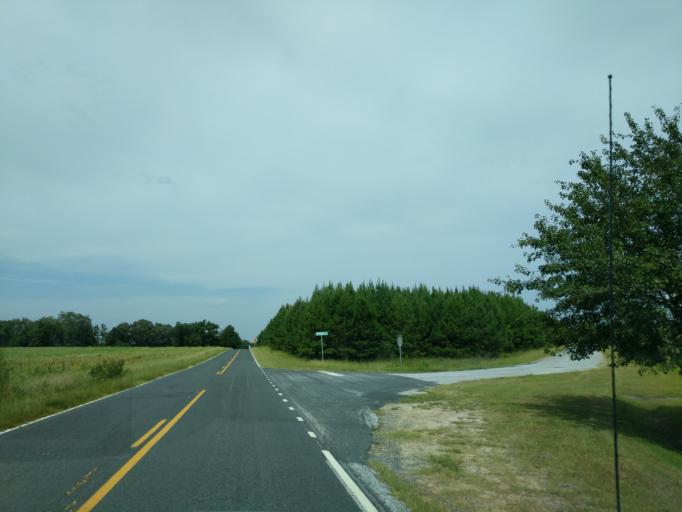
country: US
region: South Carolina
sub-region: Abbeville County
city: Lake Secession
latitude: 34.2918
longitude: -82.5387
